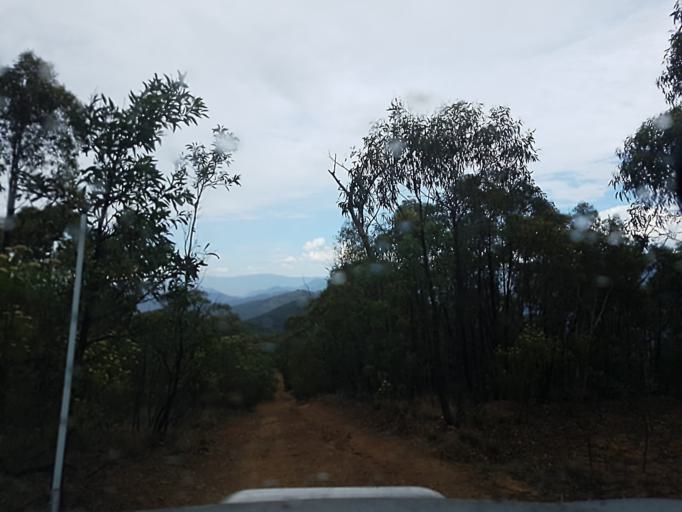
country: AU
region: New South Wales
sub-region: Snowy River
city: Jindabyne
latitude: -36.9148
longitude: 148.3363
